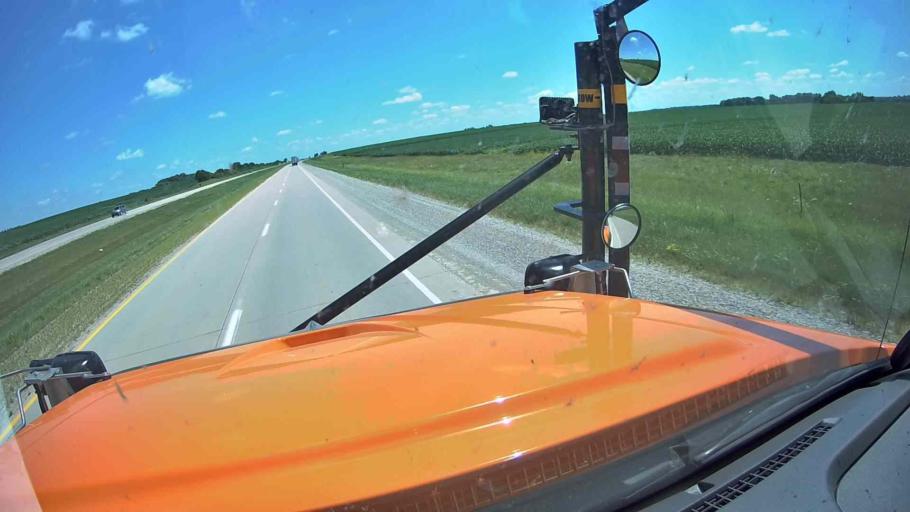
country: US
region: Iowa
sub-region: Floyd County
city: Nora Springs
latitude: 43.1188
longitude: -93.0582
